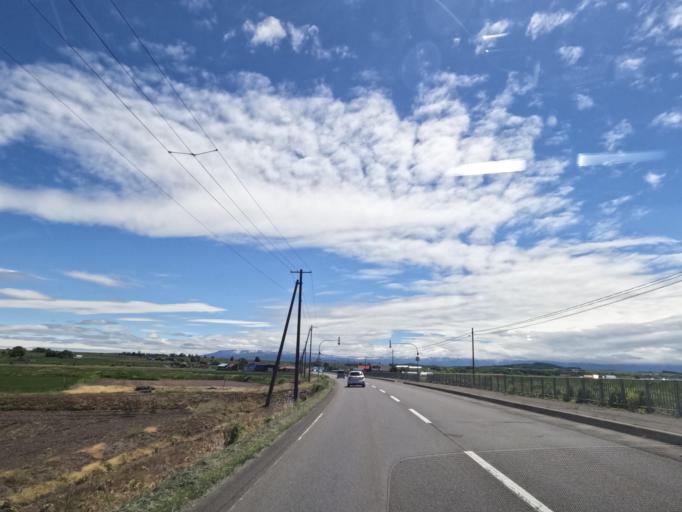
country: JP
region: Hokkaido
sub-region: Asahikawa-shi
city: Asahikawa
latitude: 43.6654
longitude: 142.4148
